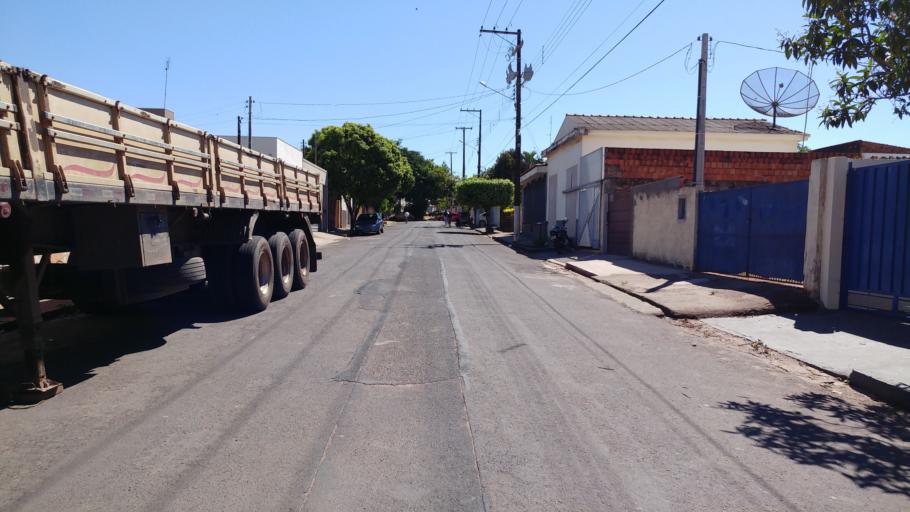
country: BR
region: Sao Paulo
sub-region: Paraguacu Paulista
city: Paraguacu Paulista
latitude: -22.4115
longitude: -50.5708
